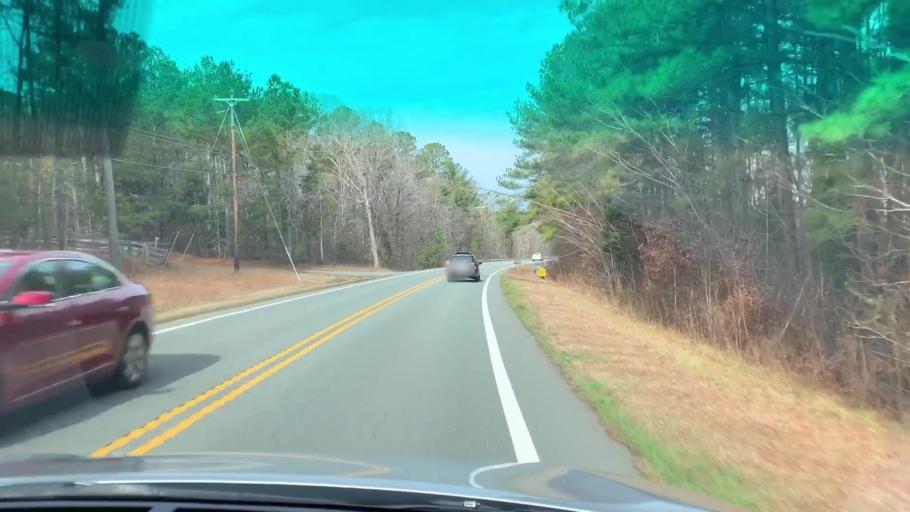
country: US
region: North Carolina
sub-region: Wake County
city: Green Level
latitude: 35.8533
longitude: -78.9387
